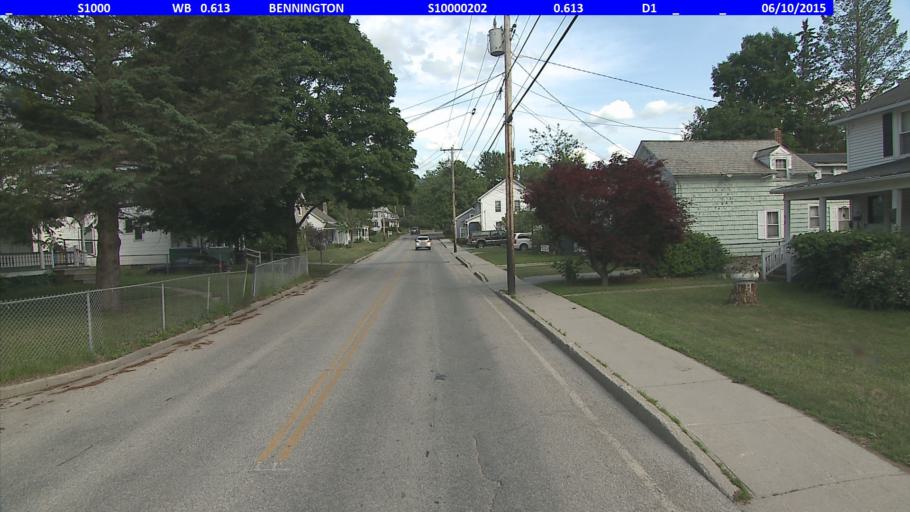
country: US
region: Vermont
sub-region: Bennington County
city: Bennington
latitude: 42.8759
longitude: -73.1833
